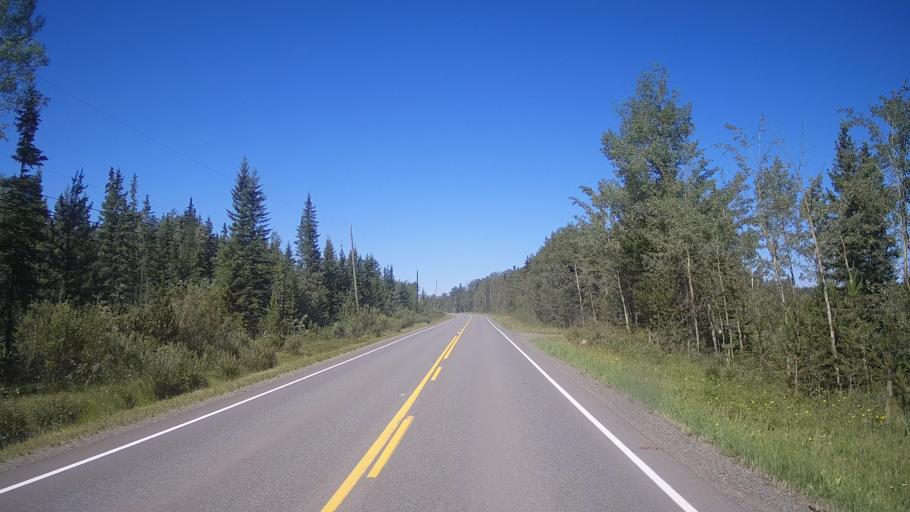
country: CA
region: British Columbia
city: Cache Creek
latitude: 51.5453
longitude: -120.9382
